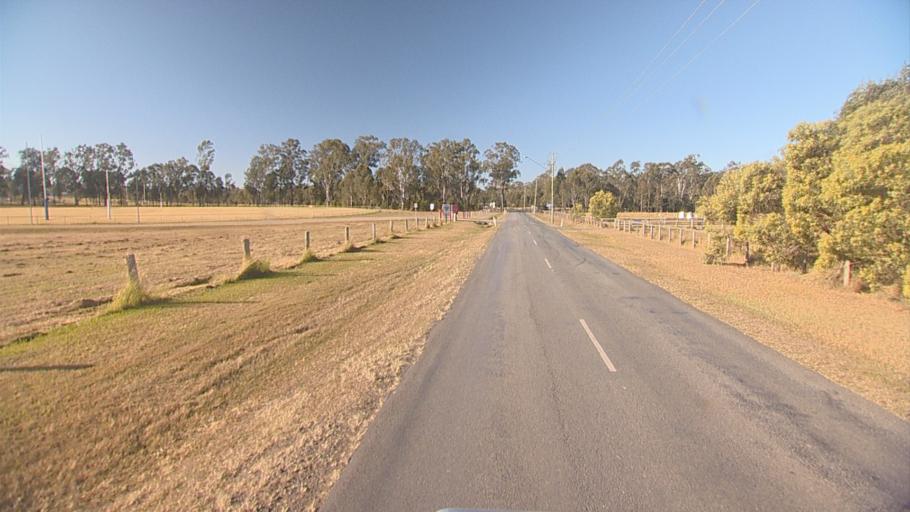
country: AU
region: Queensland
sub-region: Logan
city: North Maclean
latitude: -27.8294
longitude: 153.0120
